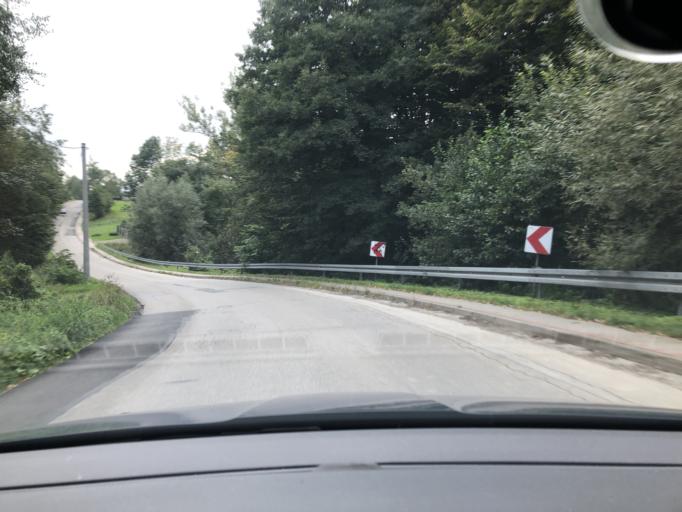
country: PL
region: Silesian Voivodeship
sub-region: Powiat zywiecki
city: Zarzecze
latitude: 49.7268
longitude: 19.1813
